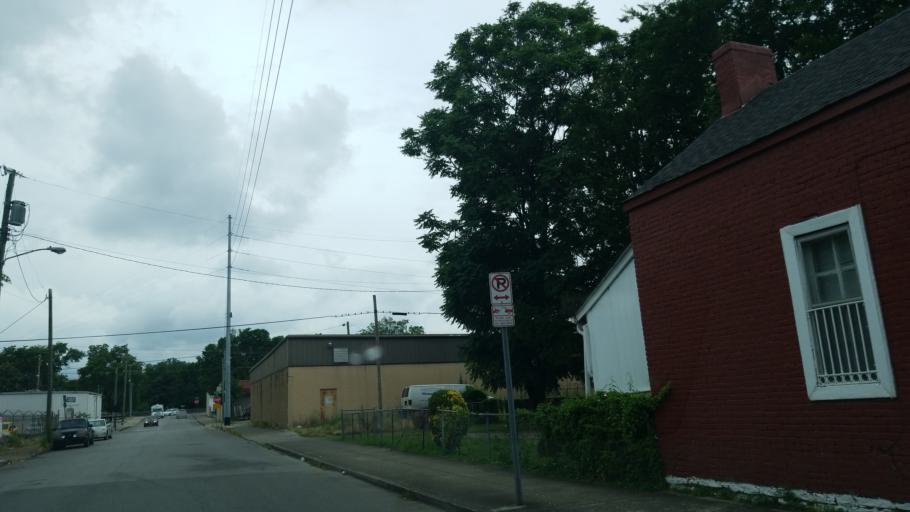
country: US
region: Tennessee
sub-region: Davidson County
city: Nashville
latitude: 36.1485
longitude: -86.7666
